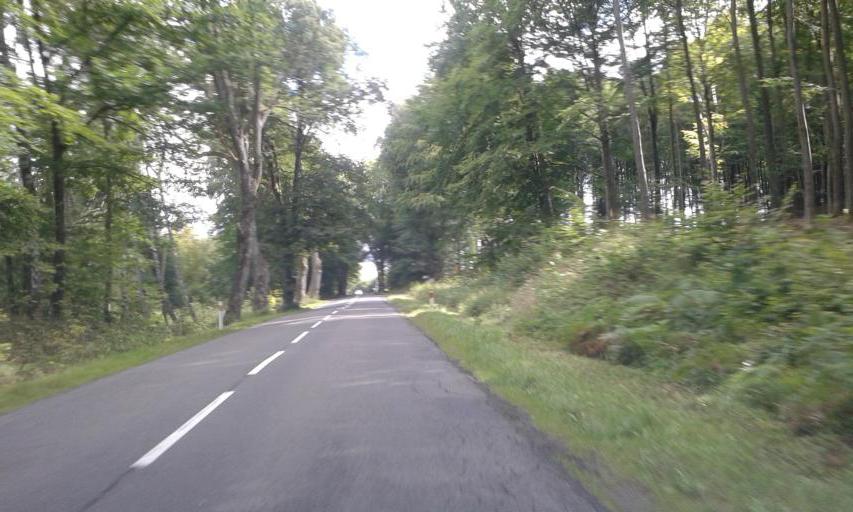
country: PL
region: West Pomeranian Voivodeship
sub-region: Powiat koszalinski
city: Bobolice
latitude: 53.9690
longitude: 16.6489
